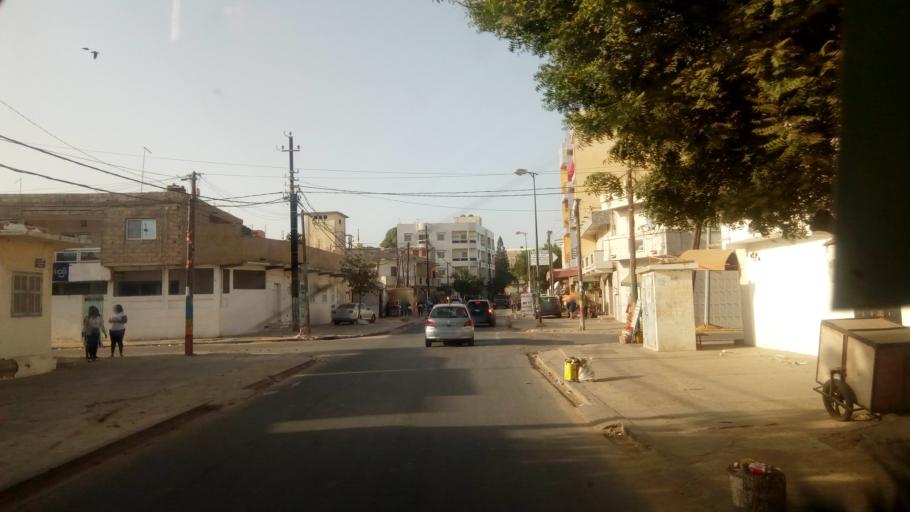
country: SN
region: Dakar
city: Grand Dakar
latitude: 14.7079
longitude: -17.4494
